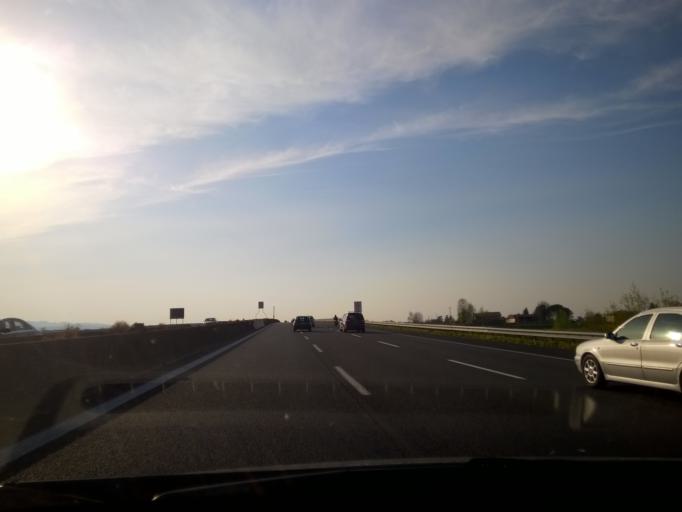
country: IT
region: Emilia-Romagna
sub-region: Provincia di Ravenna
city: Solarolo
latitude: 44.3497
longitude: 11.8291
